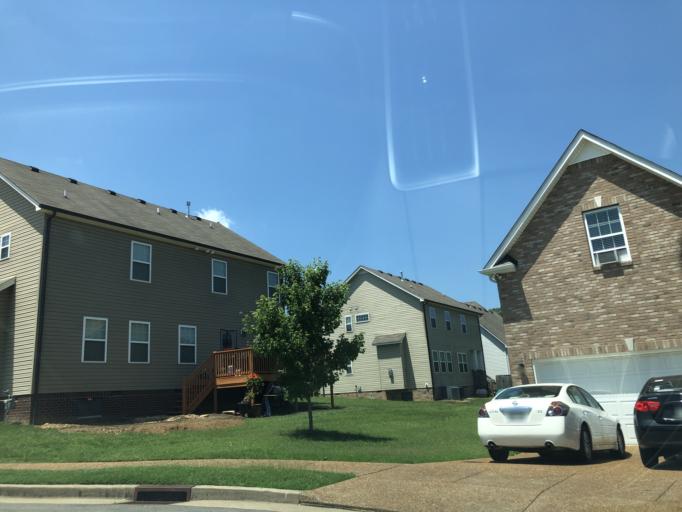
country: US
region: Tennessee
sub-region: Williamson County
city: Nolensville
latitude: 36.0166
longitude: -86.6693
